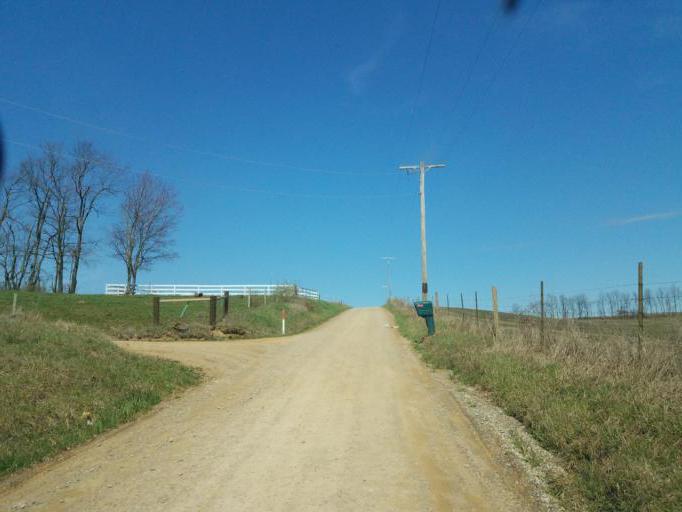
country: US
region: Ohio
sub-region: Knox County
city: Oak Hill
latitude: 40.3325
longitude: -82.1909
